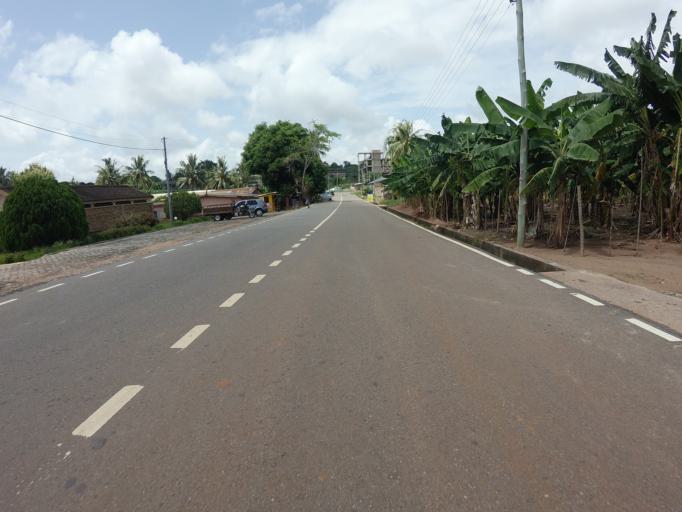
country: GH
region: Volta
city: Ho
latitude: 6.6107
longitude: 0.4574
